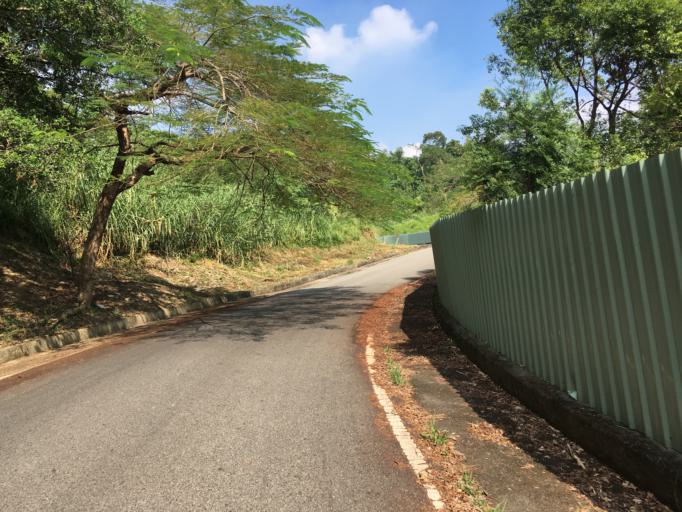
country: TW
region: Taiwan
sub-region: Taichung City
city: Taichung
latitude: 24.1776
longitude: 120.7567
